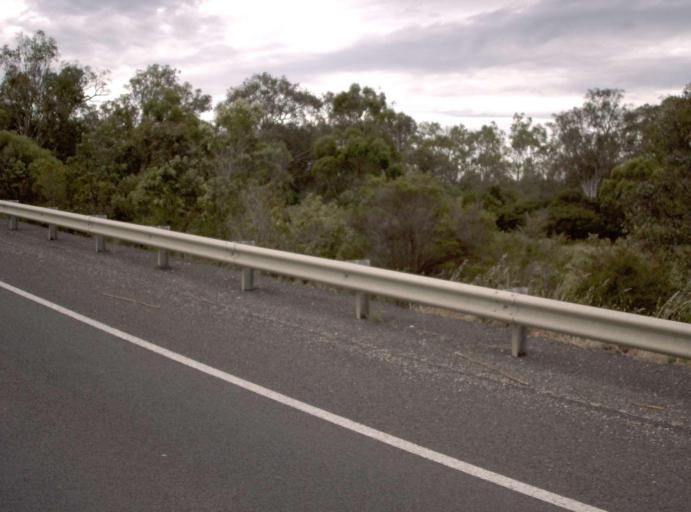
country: AU
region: Victoria
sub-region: Wellington
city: Sale
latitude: -38.1443
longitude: 147.0816
